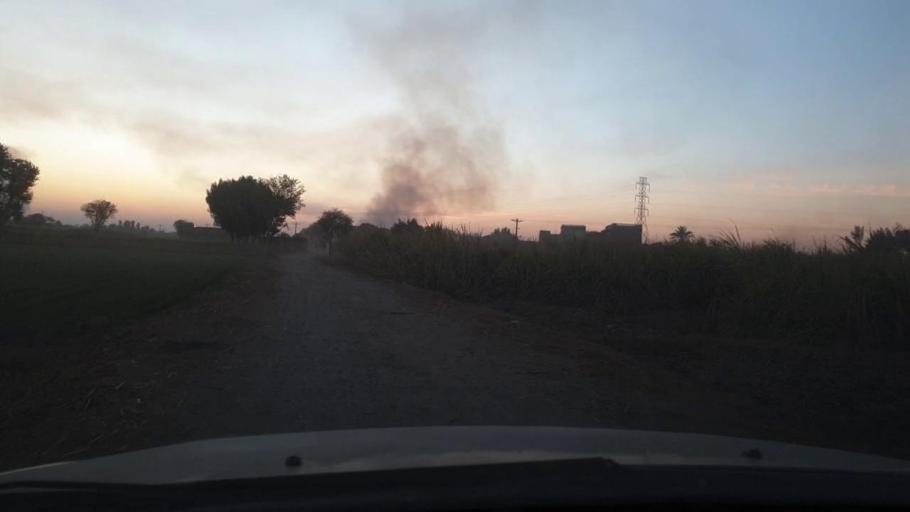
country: PK
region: Sindh
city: Ghotki
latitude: 27.9846
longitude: 69.2665
